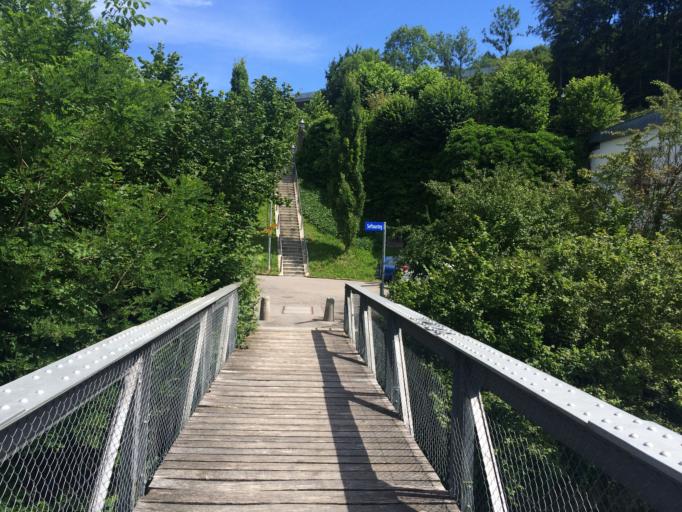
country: CH
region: Bern
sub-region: Bern-Mittelland District
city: Bern
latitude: 46.9693
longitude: 7.4390
